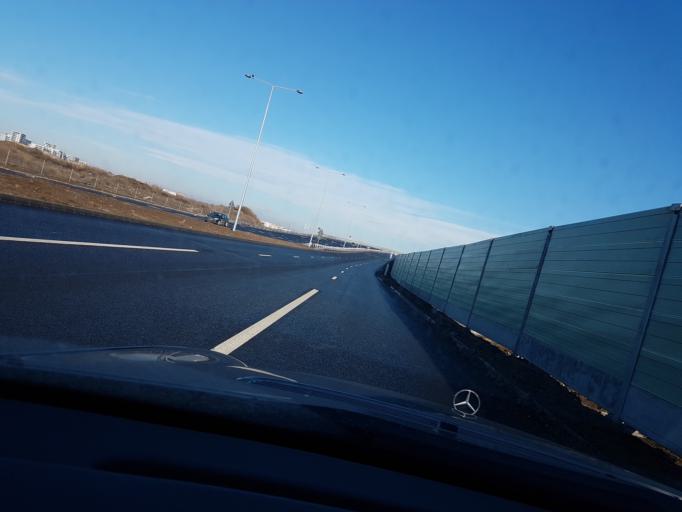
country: RO
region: Ilfov
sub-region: Comuna Fundeni-Dobroesti
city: Fundeni
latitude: 44.4793
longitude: 26.1381
